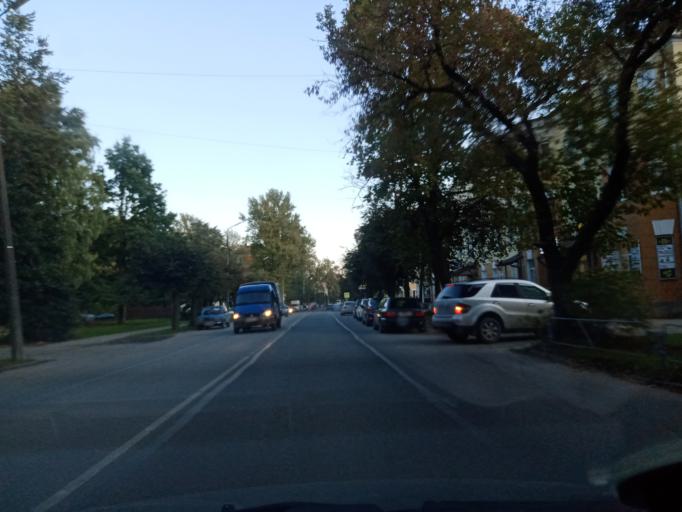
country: RU
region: Pskov
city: Pskov
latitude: 57.8066
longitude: 28.3412
